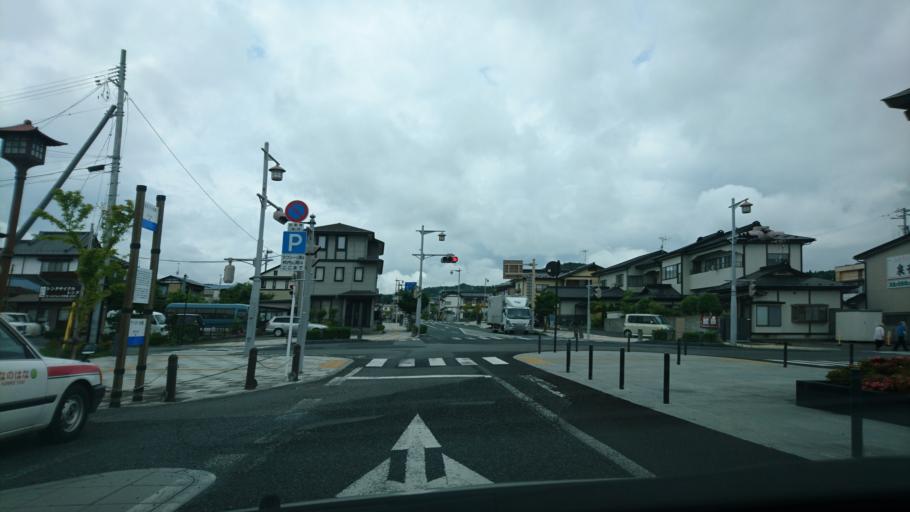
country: JP
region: Iwate
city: Ichinoseki
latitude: 38.9880
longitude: 141.1171
